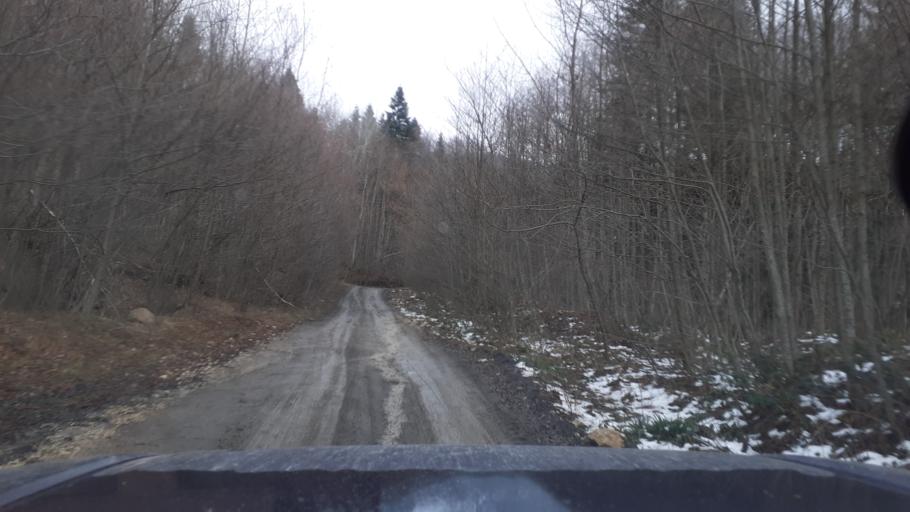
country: RU
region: Krasnodarskiy
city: Neftegorsk
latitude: 44.0807
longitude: 39.7320
